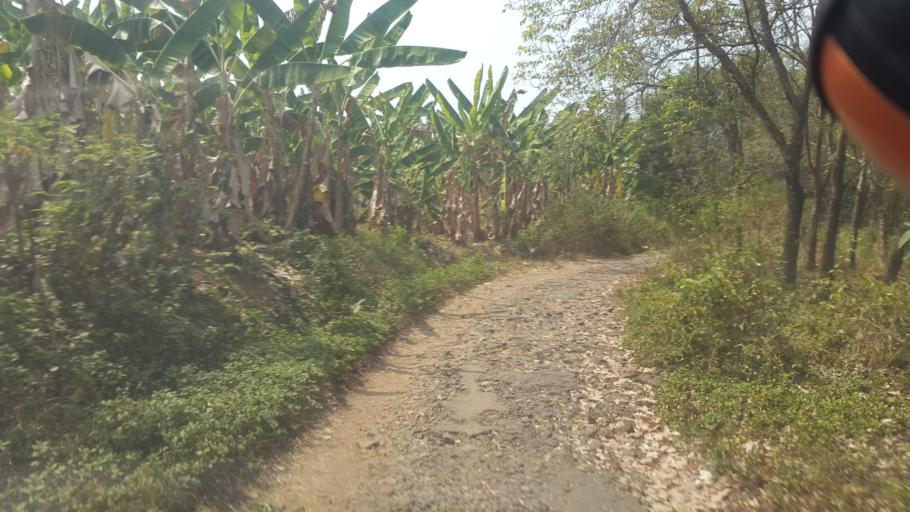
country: ID
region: West Java
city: Cimaja
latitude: -6.9327
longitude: 106.4991
